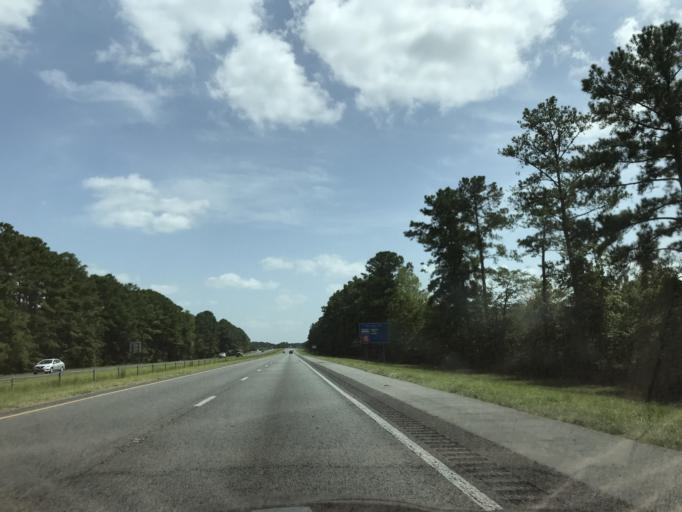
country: US
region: North Carolina
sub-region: Duplin County
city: Wallace
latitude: 34.7621
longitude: -77.9578
